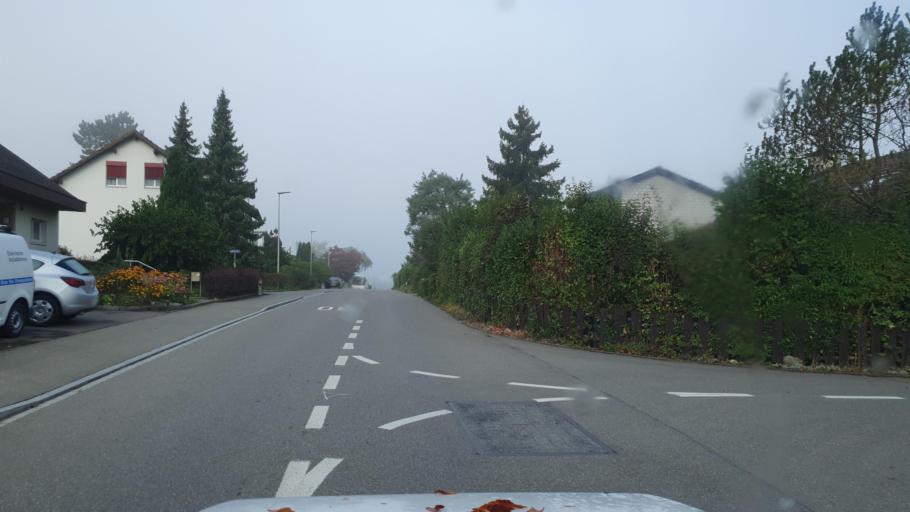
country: CH
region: Aargau
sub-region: Bezirk Baden
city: Mellingen
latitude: 47.4374
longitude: 8.2662
